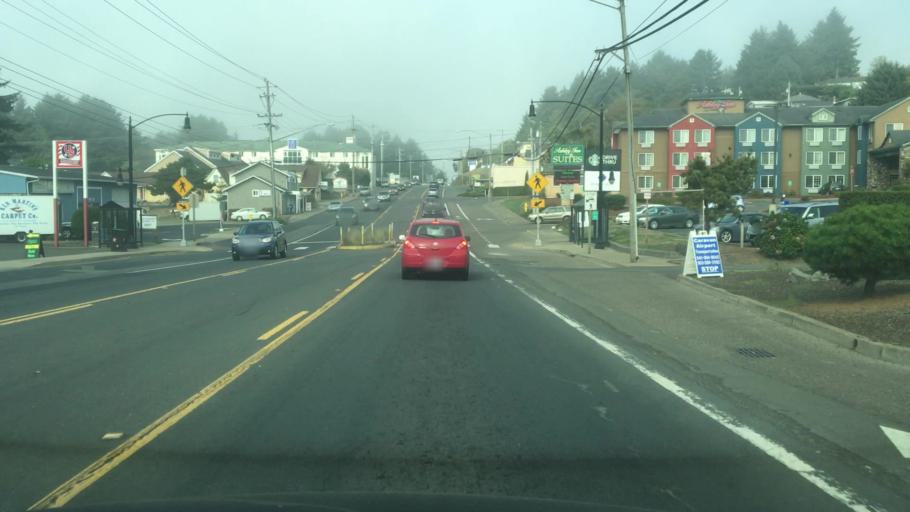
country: US
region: Oregon
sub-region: Lincoln County
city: Lincoln City
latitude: 44.9890
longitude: -124.0056
